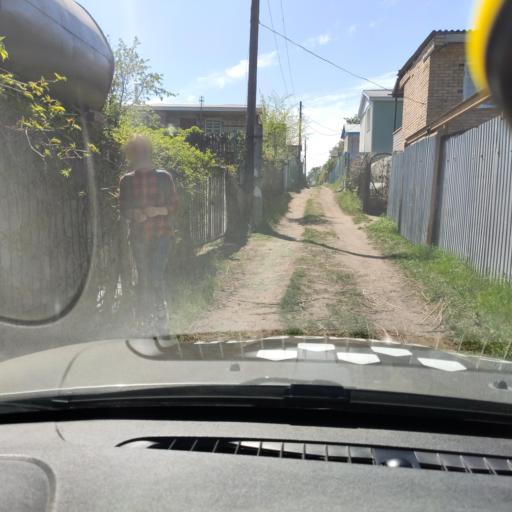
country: RU
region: Samara
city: Povolzhskiy
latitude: 53.4646
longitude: 49.6587
